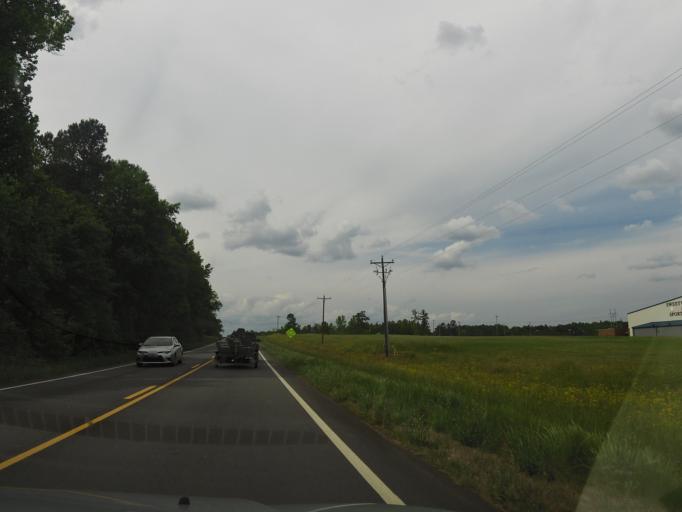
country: US
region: Georgia
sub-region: McDuffie County
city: Thomson
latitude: 33.4270
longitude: -82.4863
